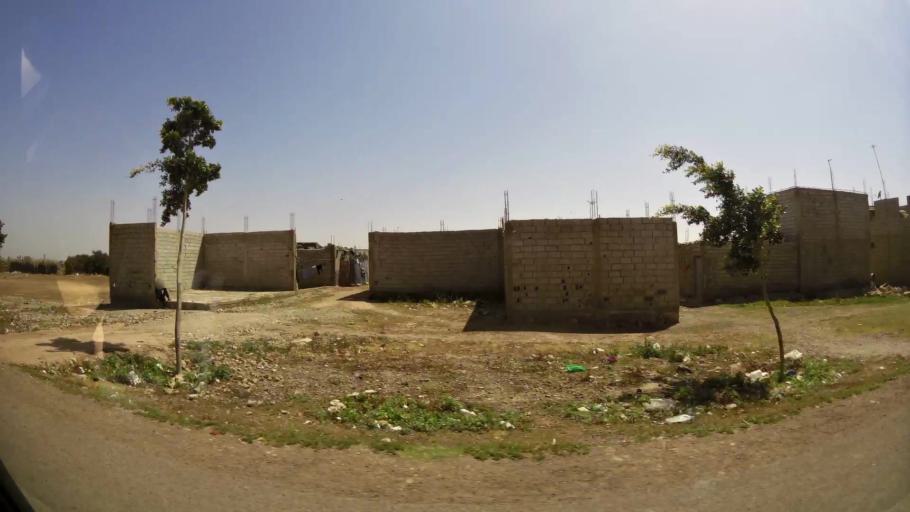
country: MA
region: Souss-Massa-Draa
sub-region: Inezgane-Ait Mellou
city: Inezgane
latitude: 30.3431
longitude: -9.5415
